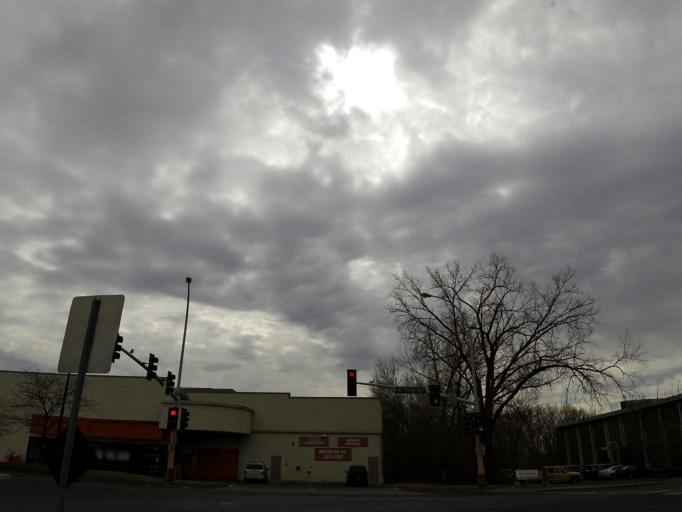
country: US
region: Minnesota
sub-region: Hennepin County
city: Edina
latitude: 44.8634
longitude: -93.3359
